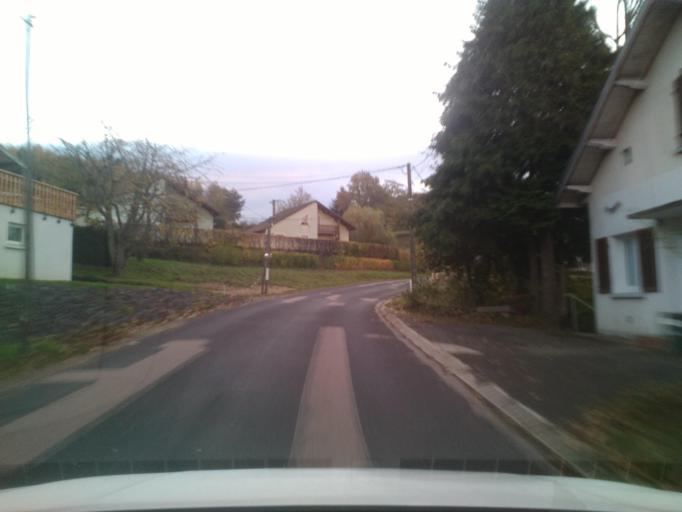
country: FR
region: Lorraine
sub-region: Departement des Vosges
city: Fraize
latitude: 48.1867
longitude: 7.0109
